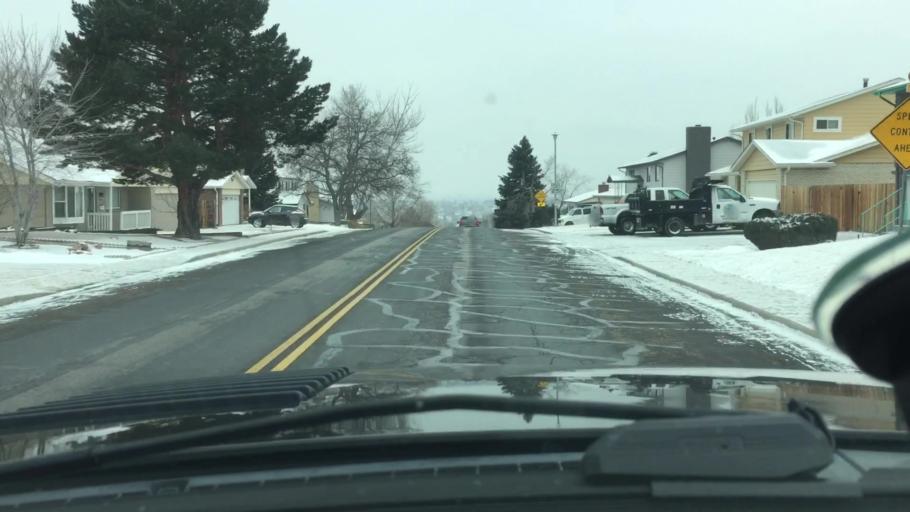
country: US
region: Colorado
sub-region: Adams County
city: Northglenn
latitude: 39.8781
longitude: -105.0056
